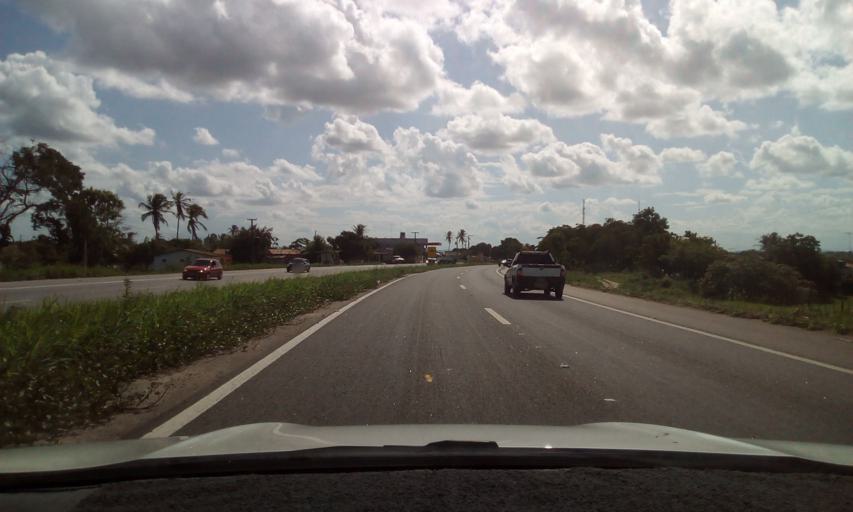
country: BR
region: Paraiba
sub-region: Pilar
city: Pilar
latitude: -7.1916
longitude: -35.2221
